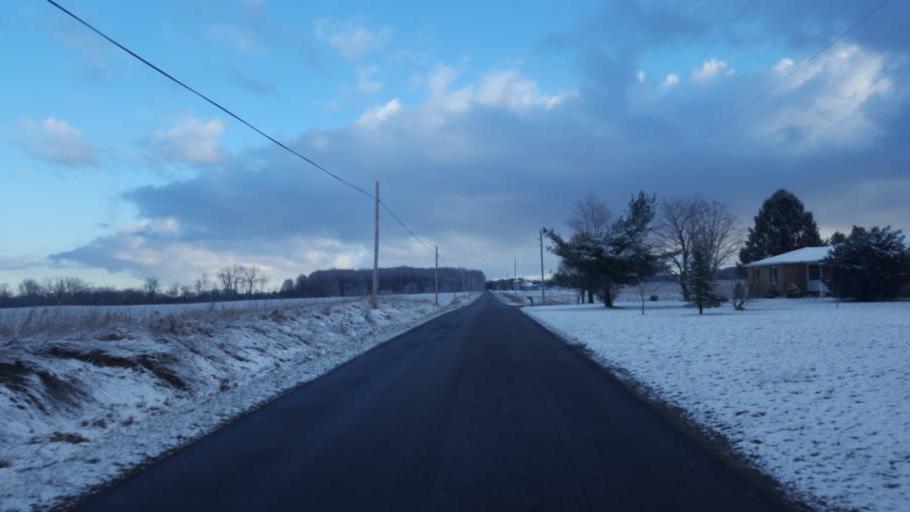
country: US
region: Ohio
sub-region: Morrow County
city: Mount Gilead
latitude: 40.5812
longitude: -82.8431
